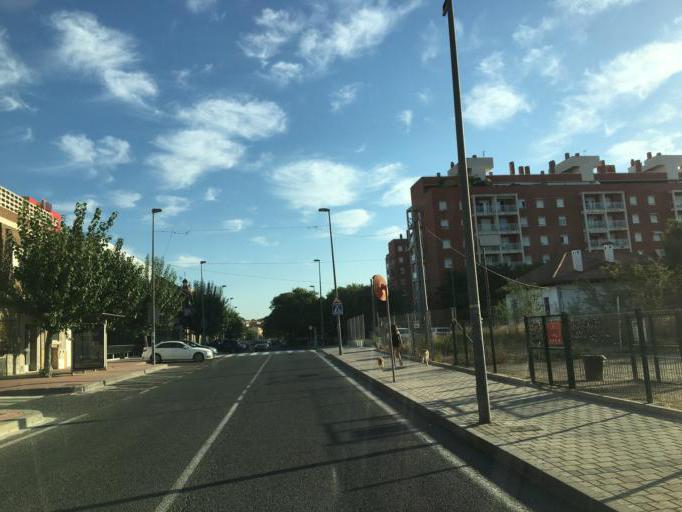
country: ES
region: Murcia
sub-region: Murcia
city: Murcia
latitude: 38.0134
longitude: -1.1508
